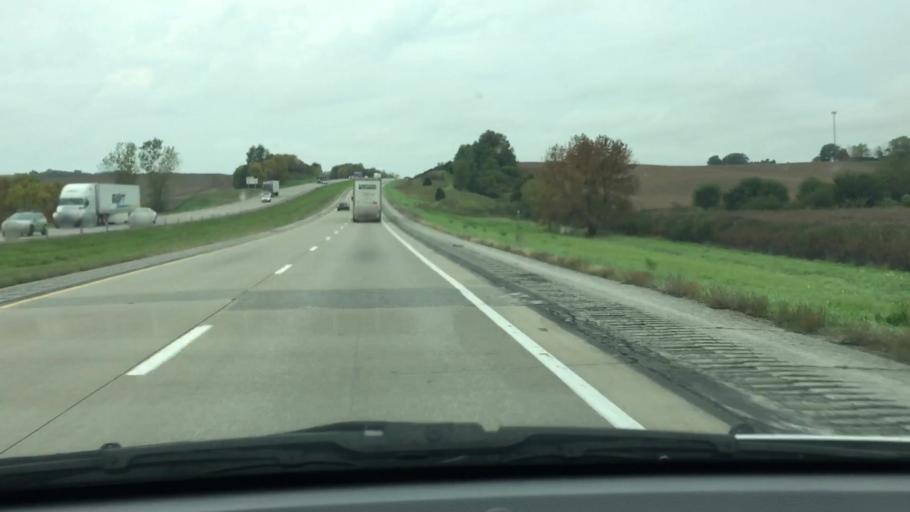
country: US
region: Iowa
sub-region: Cedar County
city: West Branch
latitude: 41.6674
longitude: -91.3888
